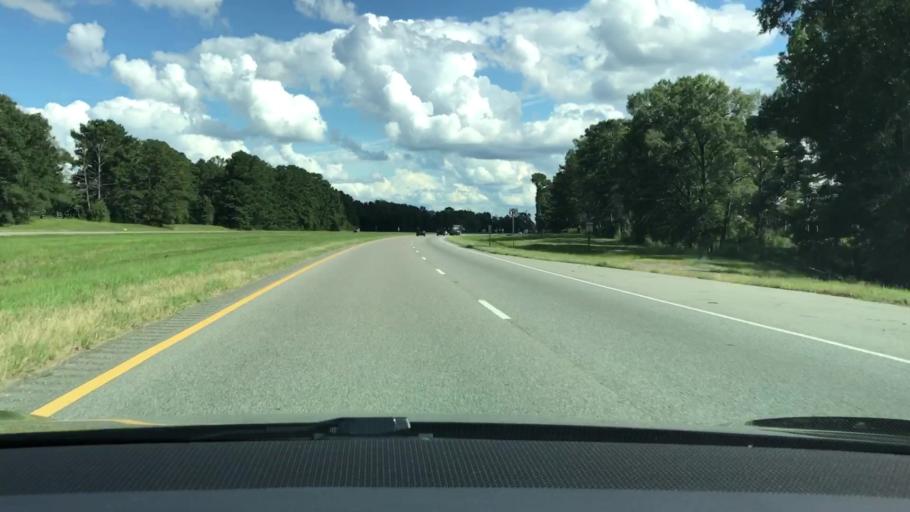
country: US
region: Alabama
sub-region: Montgomery County
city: Taylor
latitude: 32.0441
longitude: -86.0365
